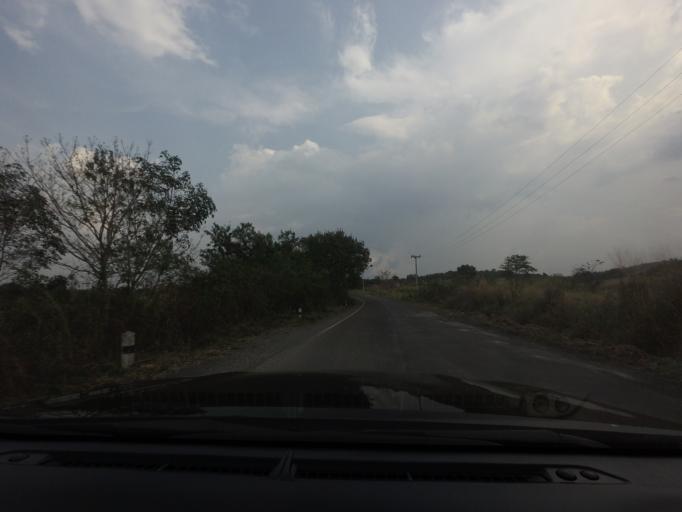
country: TH
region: Nakhon Ratchasima
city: Wang Nam Khiao
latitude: 14.4110
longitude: 101.7714
